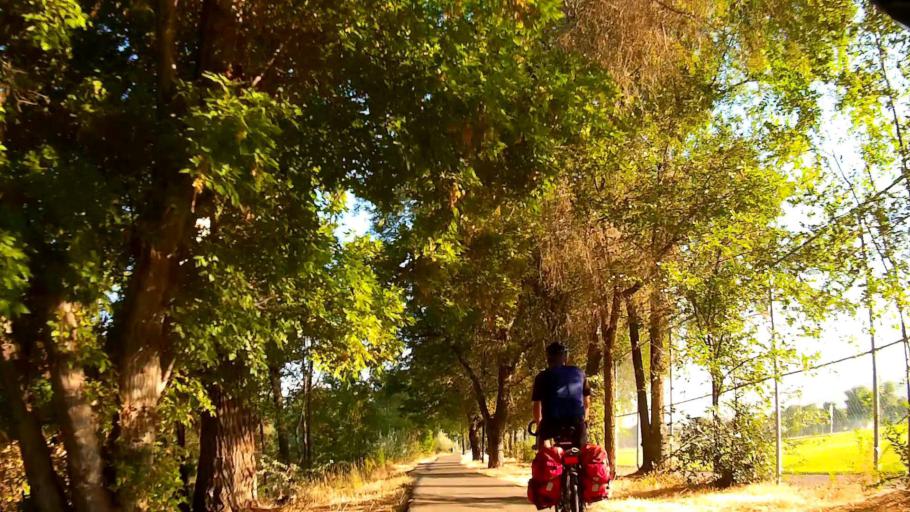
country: US
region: Utah
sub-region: Salt Lake County
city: Salt Lake City
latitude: 40.7828
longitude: -111.9361
